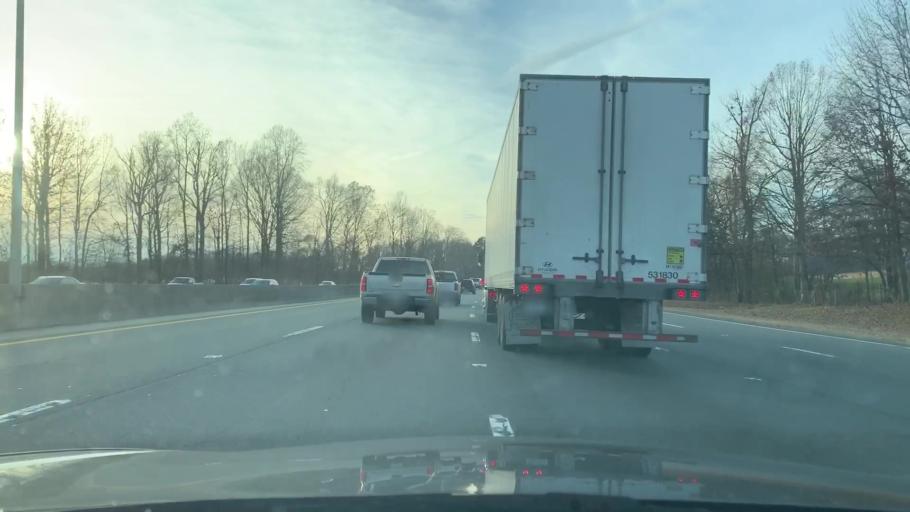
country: US
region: North Carolina
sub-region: Alamance County
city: Haw River
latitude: 36.0657
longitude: -79.3171
